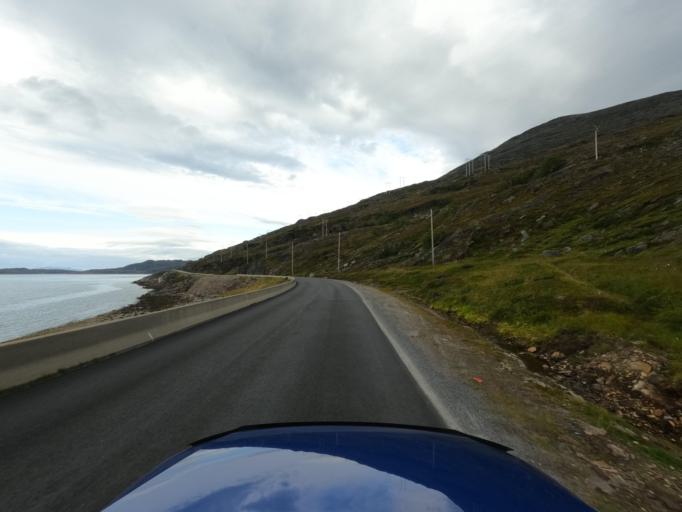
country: NO
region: Finnmark Fylke
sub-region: Hammerfest
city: Rypefjord
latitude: 70.5693
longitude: 23.6972
